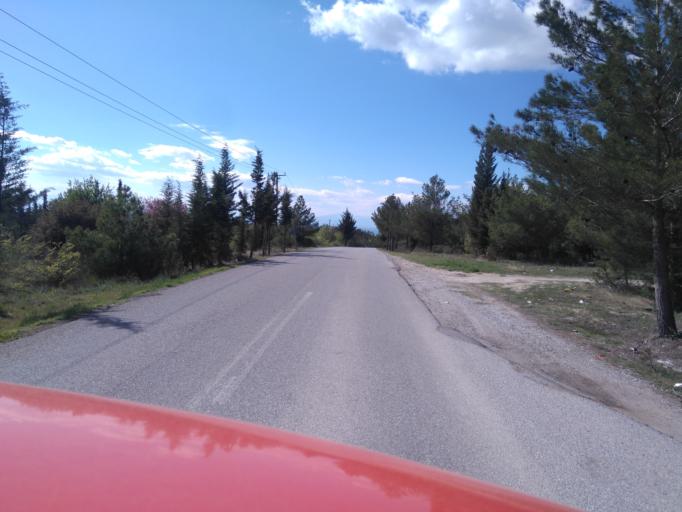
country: GR
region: Central Macedonia
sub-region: Nomos Thessalonikis
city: Pefka
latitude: 40.6456
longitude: 22.9937
